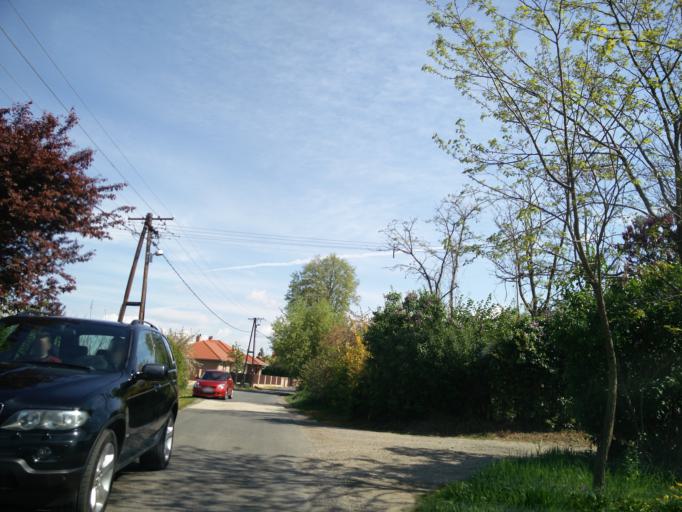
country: HU
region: Zala
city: Zalaegerszeg
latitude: 46.8060
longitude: 16.8365
